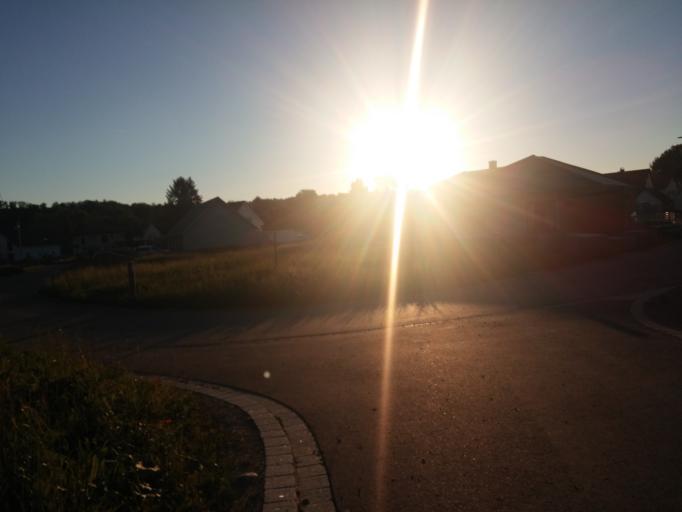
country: DE
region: Bavaria
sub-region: Swabia
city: Lautrach
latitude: 47.8992
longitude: 10.1265
